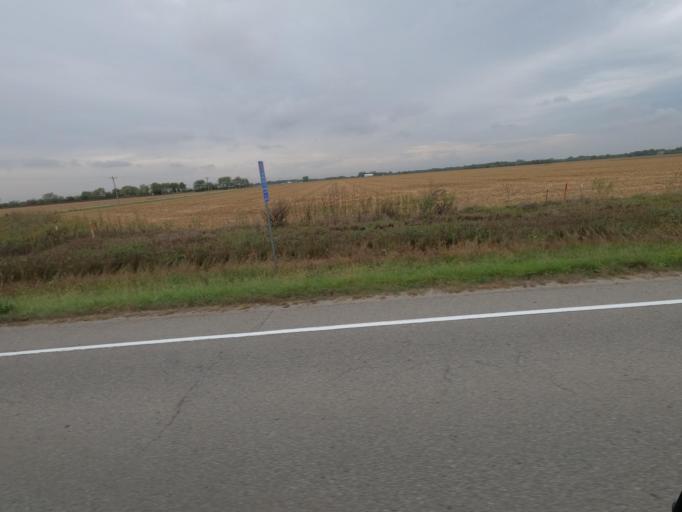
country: US
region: Iowa
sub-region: Van Buren County
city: Keosauqua
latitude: 40.8136
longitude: -91.8999
